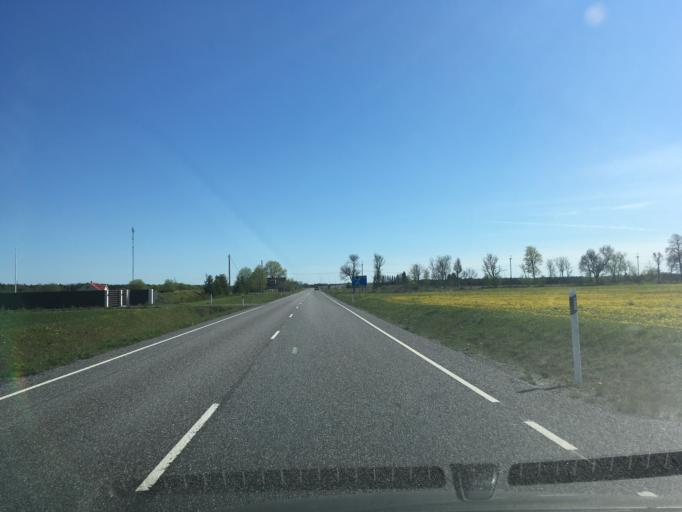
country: EE
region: Harju
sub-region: Rae vald
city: Vaida
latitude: 59.2582
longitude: 25.0178
